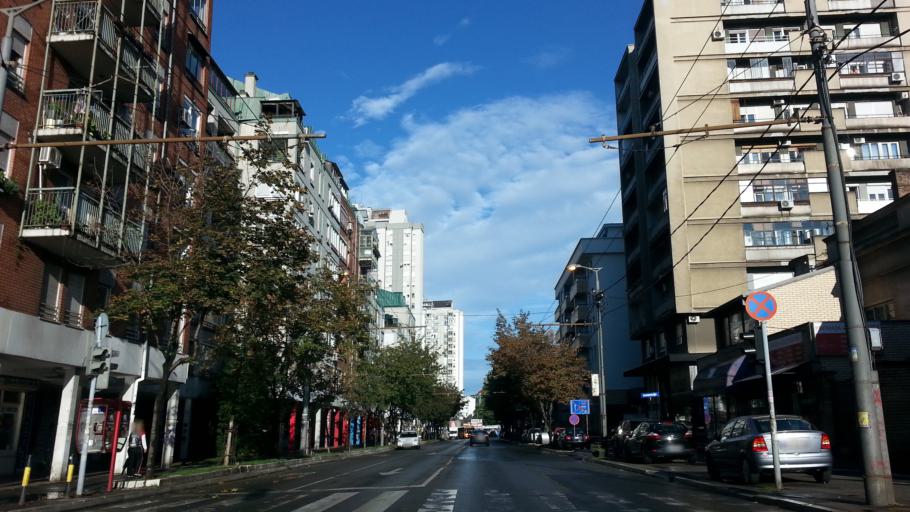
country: RS
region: Central Serbia
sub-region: Belgrade
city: Vracar
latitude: 44.7942
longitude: 20.4930
